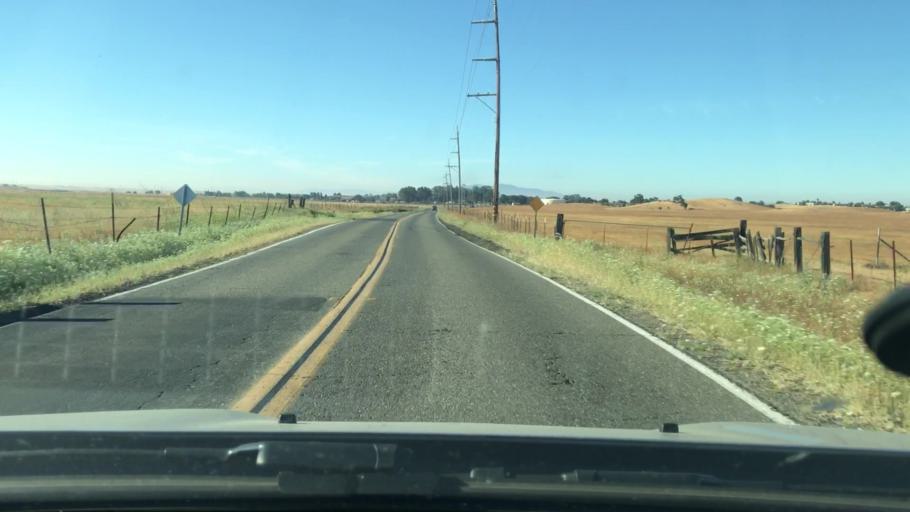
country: US
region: California
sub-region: Solano County
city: Vacaville
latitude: 38.2978
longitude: -121.9337
